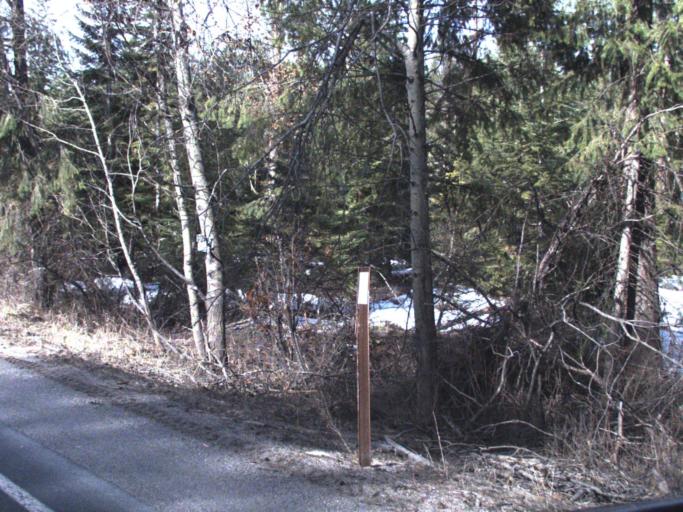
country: US
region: Washington
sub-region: Stevens County
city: Colville
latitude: 48.5092
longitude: -117.7028
